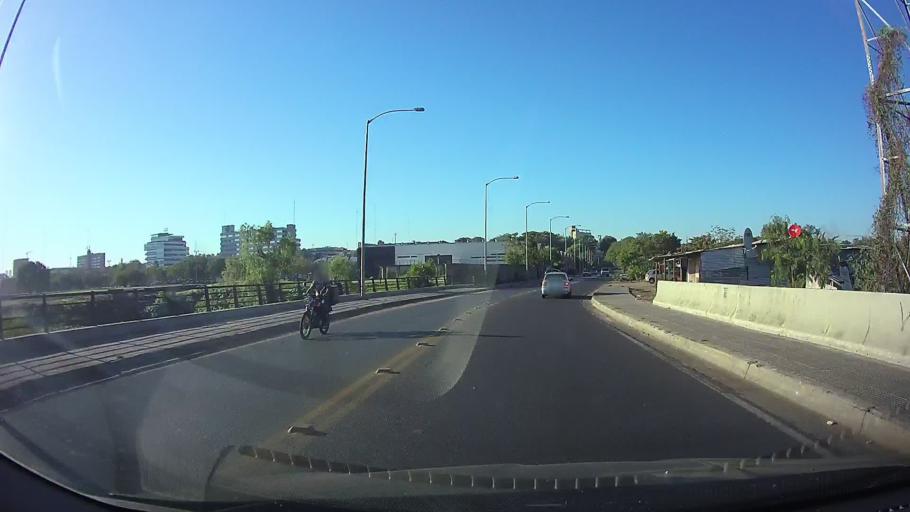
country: PY
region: Asuncion
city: Asuncion
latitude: -25.2713
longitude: -57.6122
